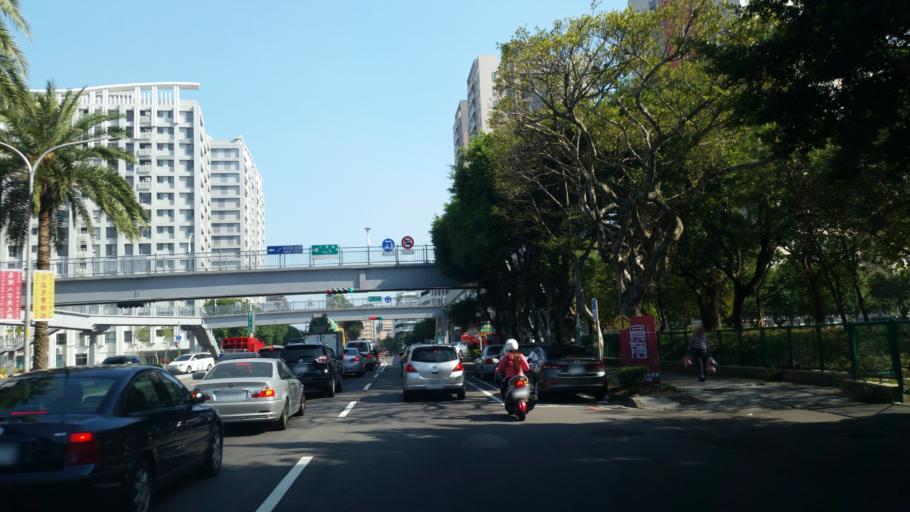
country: TW
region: Taiwan
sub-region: Taoyuan
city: Taoyuan
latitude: 25.0739
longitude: 121.3772
